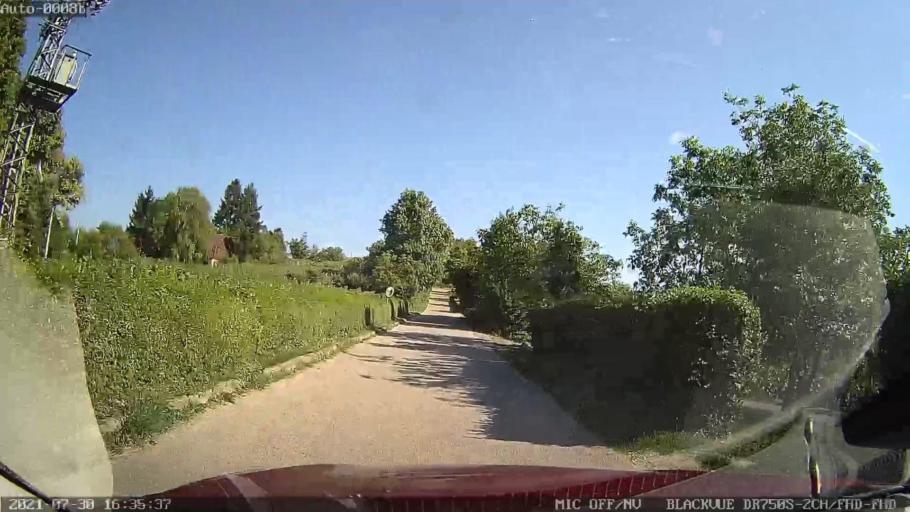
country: HR
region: Varazdinska
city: Jalzabet
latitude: 46.2445
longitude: 16.4752
